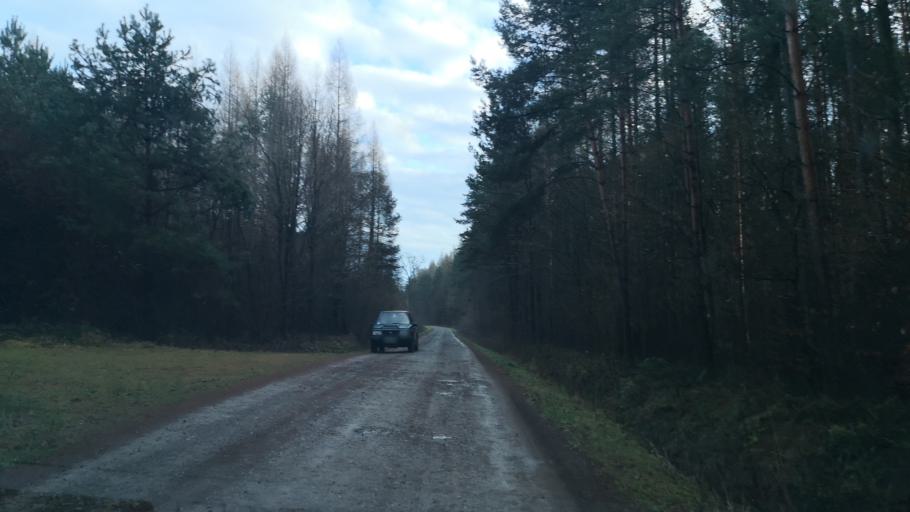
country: PL
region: Subcarpathian Voivodeship
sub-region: Powiat lezajski
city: Piskorowice
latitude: 50.2536
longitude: 22.5638
